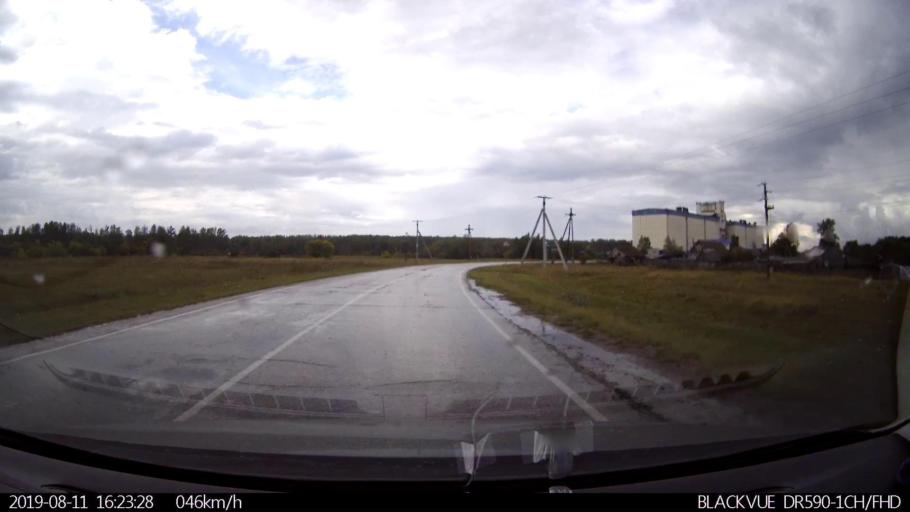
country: RU
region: Ulyanovsk
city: Mayna
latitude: 54.0953
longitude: 47.5885
